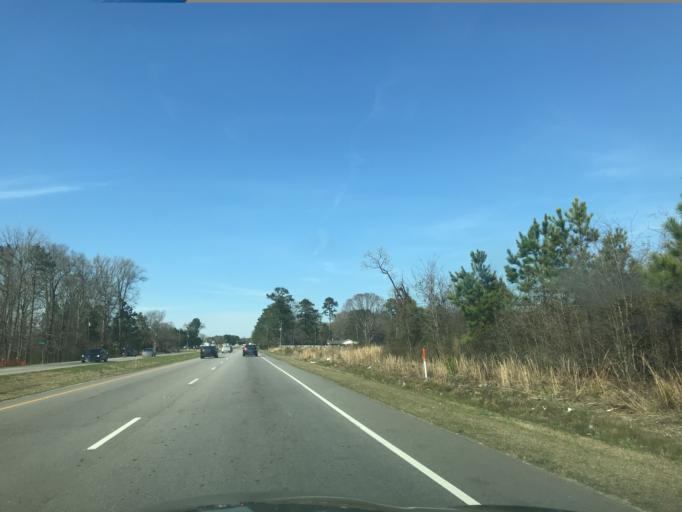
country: US
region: North Carolina
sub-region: Wake County
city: Garner
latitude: 35.6564
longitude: -78.7049
